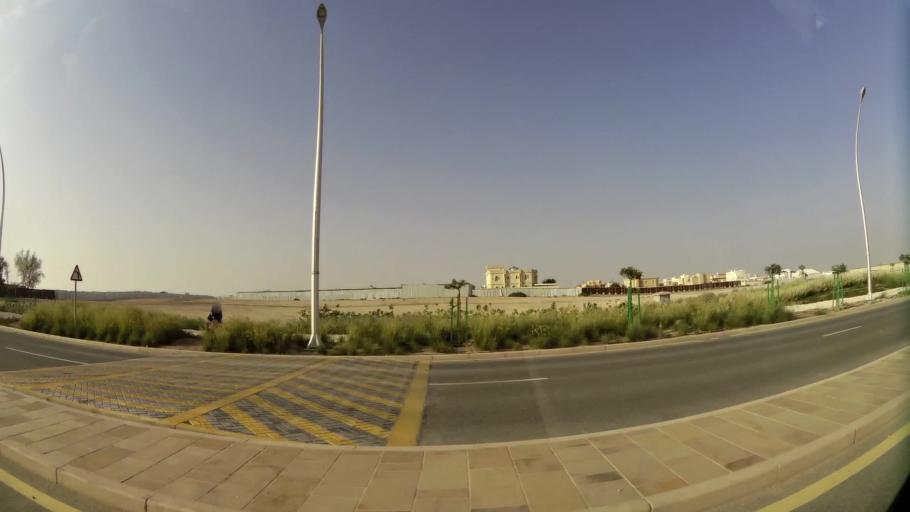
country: QA
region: Baladiyat ar Rayyan
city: Ar Rayyan
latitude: 25.3298
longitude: 51.4318
